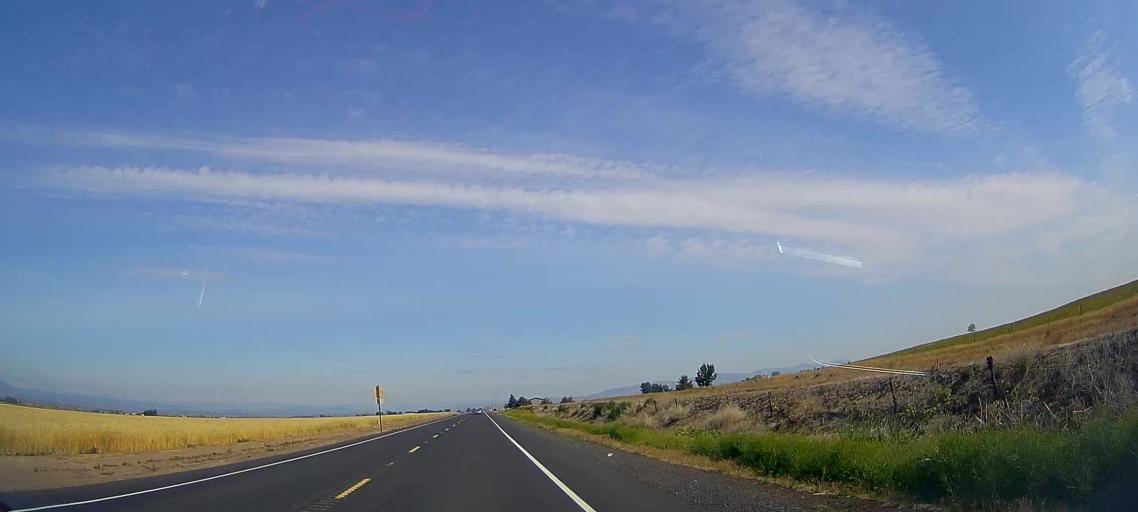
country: US
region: Oregon
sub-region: Jefferson County
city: Madras
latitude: 44.6712
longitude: -121.1406
